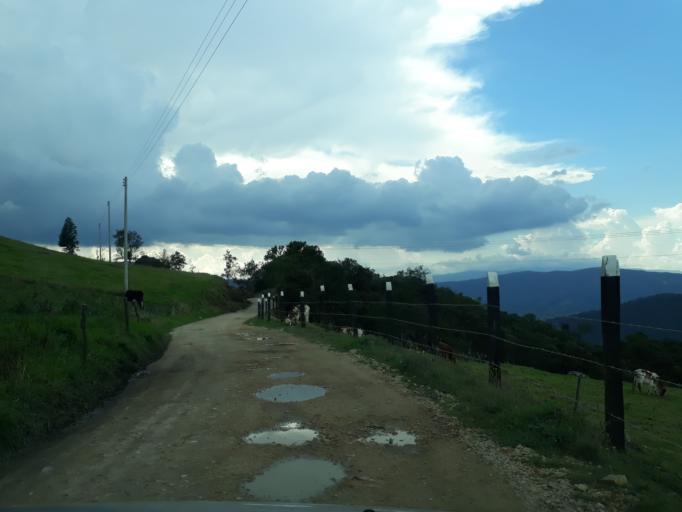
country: CO
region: Cundinamarca
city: Lenguazaque
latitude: 5.2558
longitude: -73.6854
